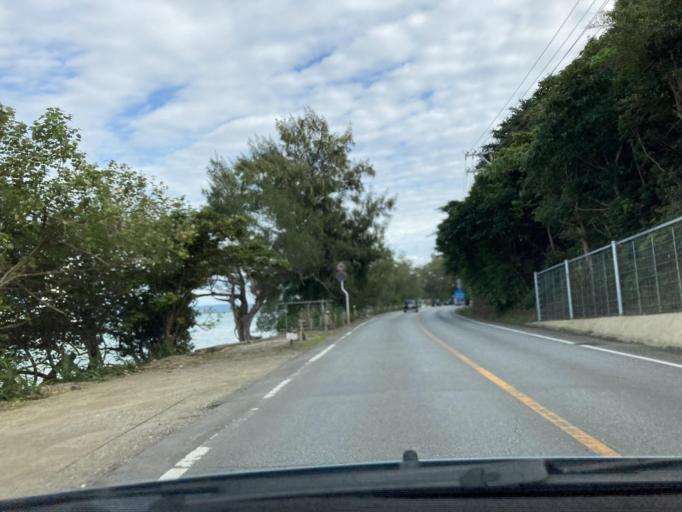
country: JP
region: Okinawa
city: Nago
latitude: 26.6455
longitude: 127.9935
